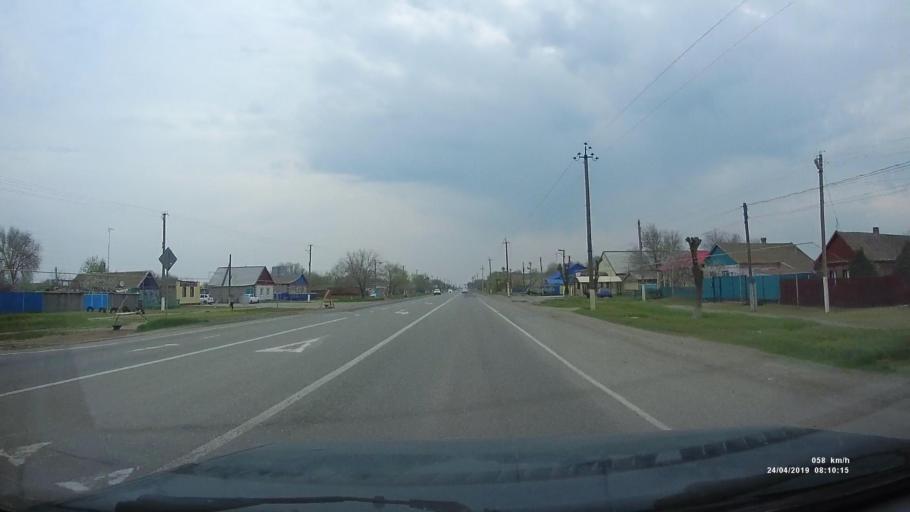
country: RU
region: Kalmykiya
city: Priyutnoye
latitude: 46.0983
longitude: 43.5144
